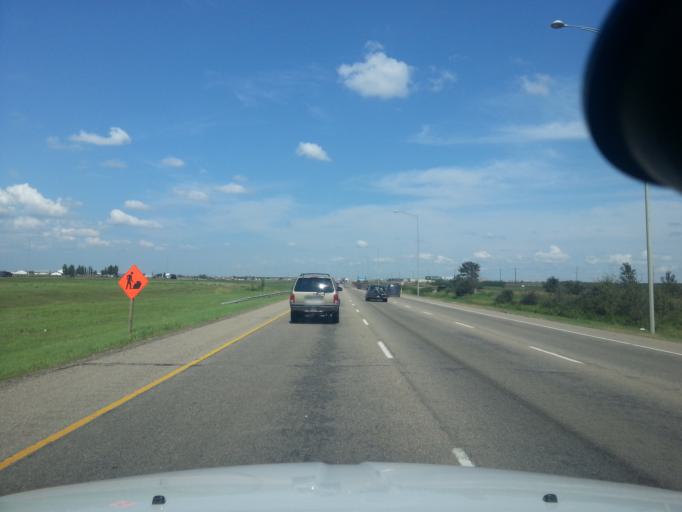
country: CA
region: Alberta
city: Beaumont
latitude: 53.3781
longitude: -113.5209
